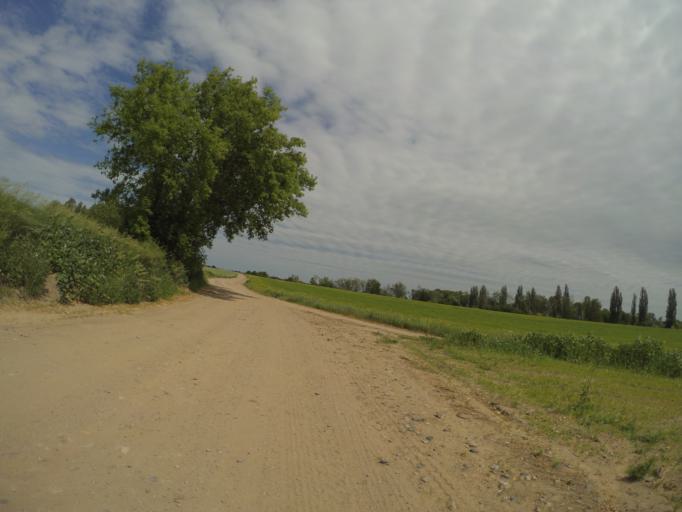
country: CZ
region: Central Bohemia
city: Lysa nad Labem
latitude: 50.1818
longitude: 14.8287
